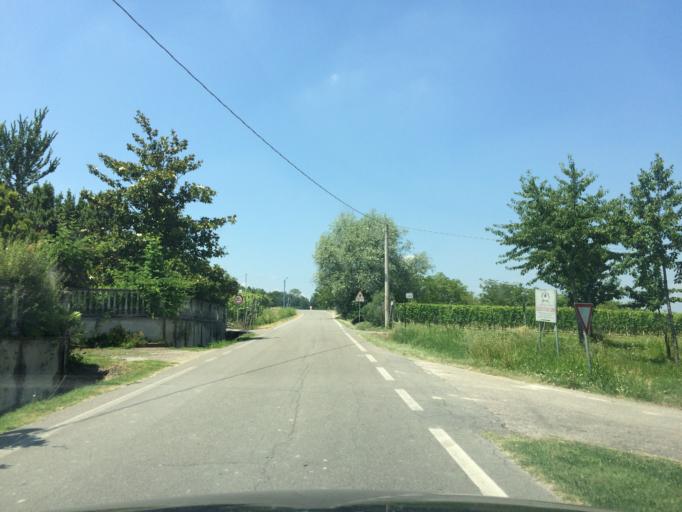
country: IT
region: Piedmont
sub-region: Provincia di Asti
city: Calosso
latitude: 44.7450
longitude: 8.2370
